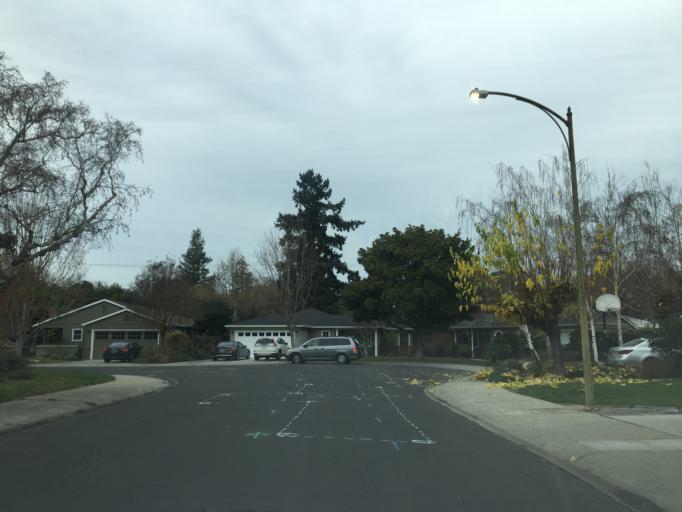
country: US
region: California
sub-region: Santa Clara County
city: Palo Alto
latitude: 37.4370
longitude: -122.1303
